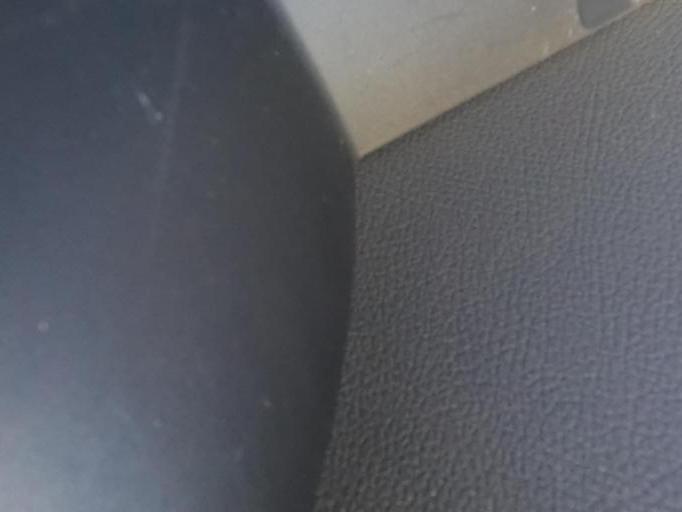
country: CA
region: Yukon
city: Dawson City
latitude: 64.0638
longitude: -139.4257
